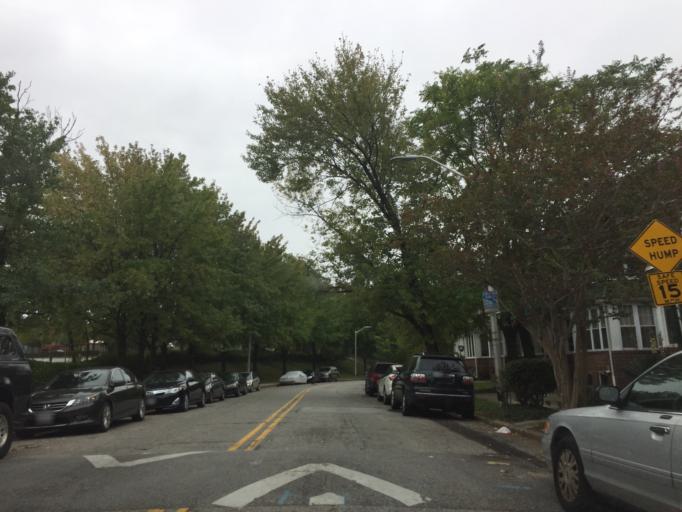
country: US
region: Maryland
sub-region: City of Baltimore
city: Baltimore
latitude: 39.3280
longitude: -76.6036
